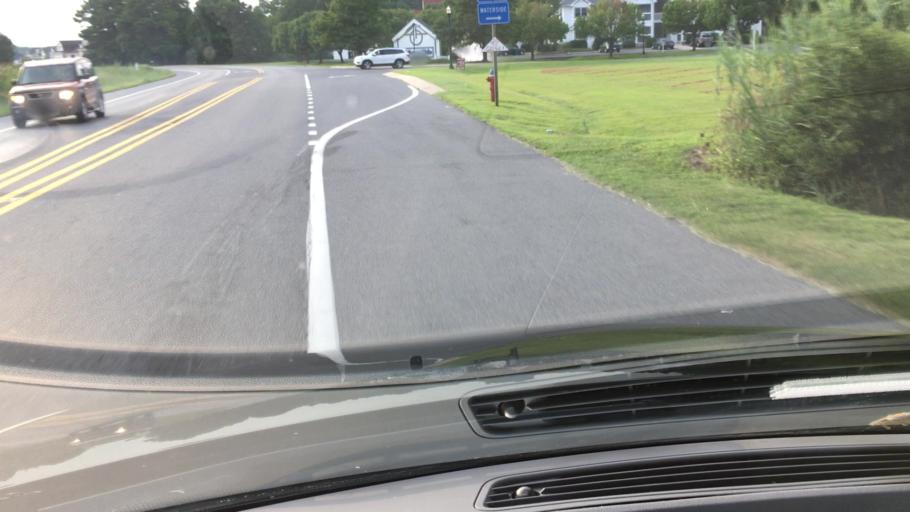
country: US
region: Delaware
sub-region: Sussex County
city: Bethany Beach
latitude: 38.5242
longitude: -75.0725
